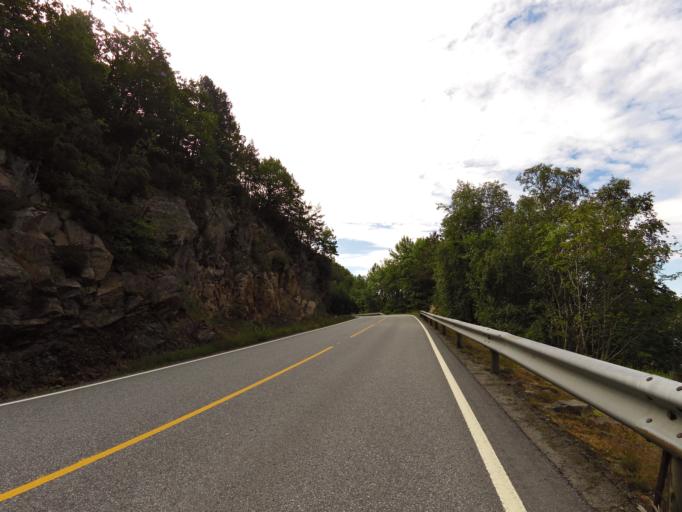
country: NO
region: Vest-Agder
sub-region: Lindesnes
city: Vigeland
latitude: 58.0566
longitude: 7.1809
